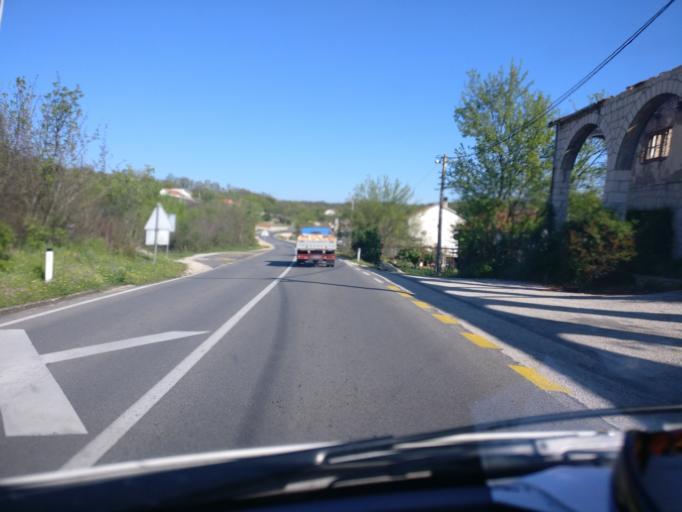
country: BA
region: Federation of Bosnia and Herzegovina
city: Crnici
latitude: 43.1055
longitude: 17.9067
